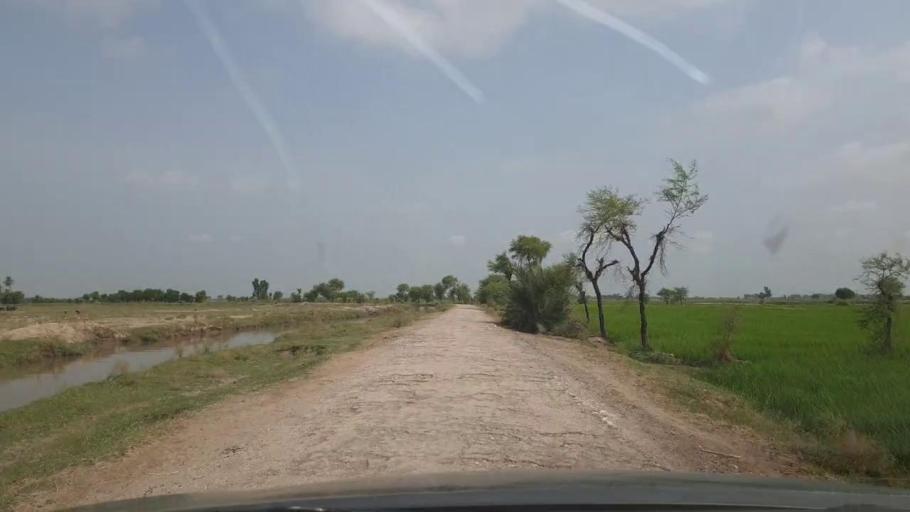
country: PK
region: Sindh
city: Ratodero
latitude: 27.8441
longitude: 68.3081
